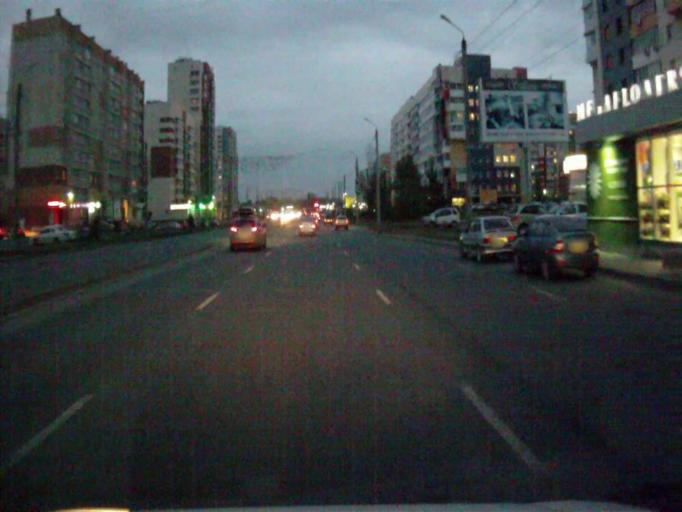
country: RU
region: Chelyabinsk
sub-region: Gorod Chelyabinsk
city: Chelyabinsk
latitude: 55.1664
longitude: 61.2948
